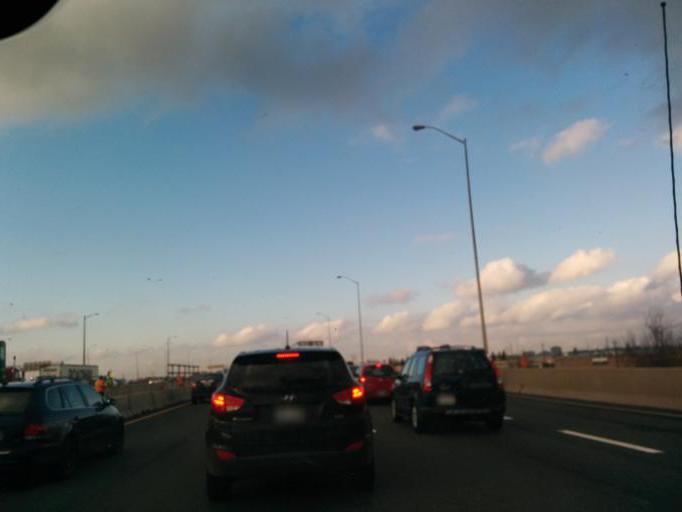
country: CA
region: Ontario
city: Etobicoke
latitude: 43.7015
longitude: -79.6098
